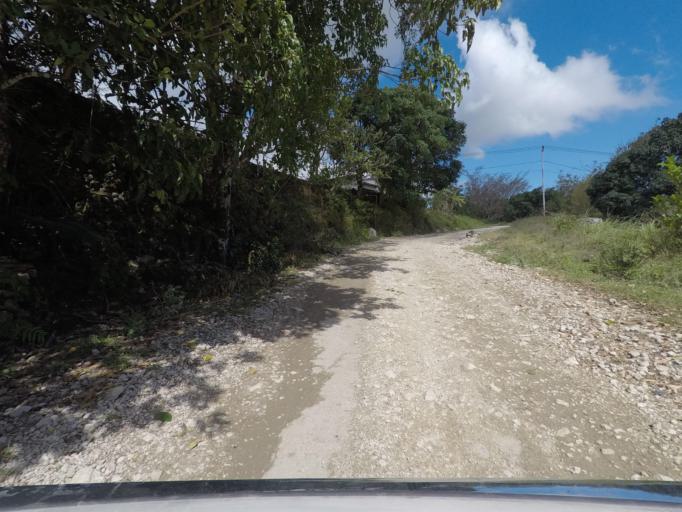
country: TL
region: Baucau
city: Venilale
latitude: -8.6853
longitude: 126.3733
